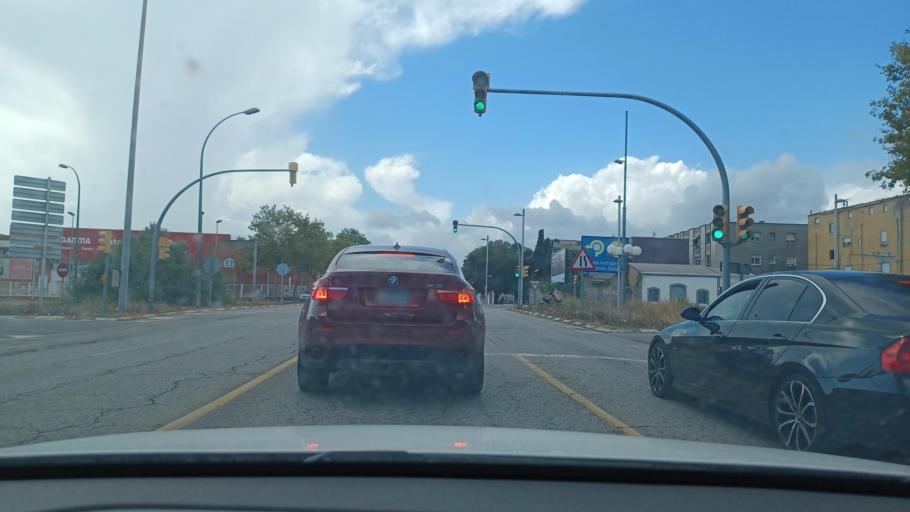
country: ES
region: Catalonia
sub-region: Provincia de Tarragona
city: Tarragona
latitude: 41.1154
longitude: 1.2223
